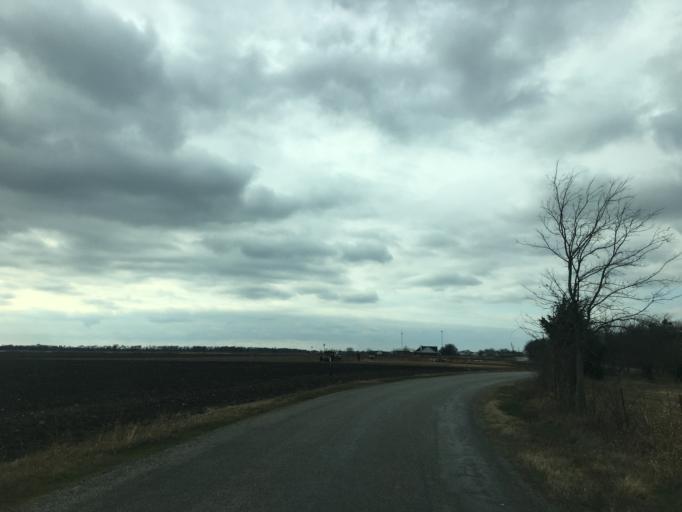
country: US
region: Texas
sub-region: Ellis County
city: Palmer
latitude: 32.4602
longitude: -96.6496
